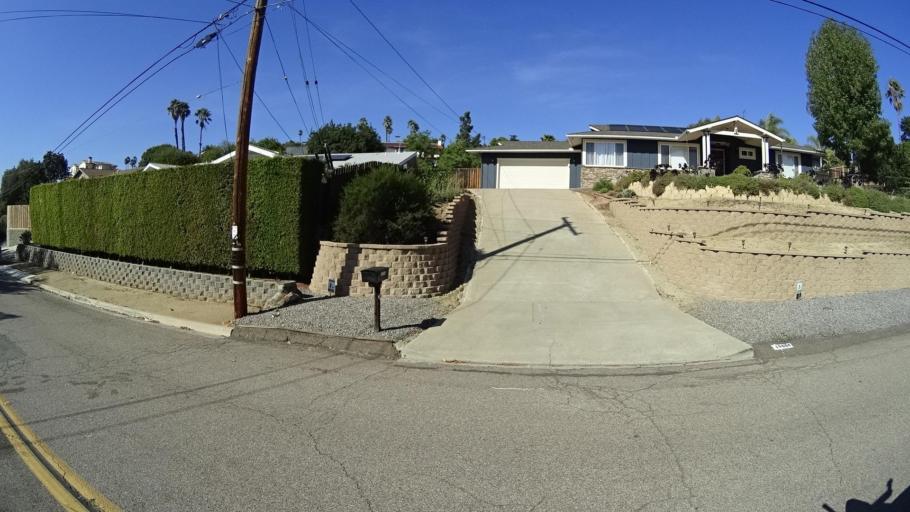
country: US
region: California
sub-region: San Diego County
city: Casa de Oro-Mount Helix
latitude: 32.7580
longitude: -116.9780
